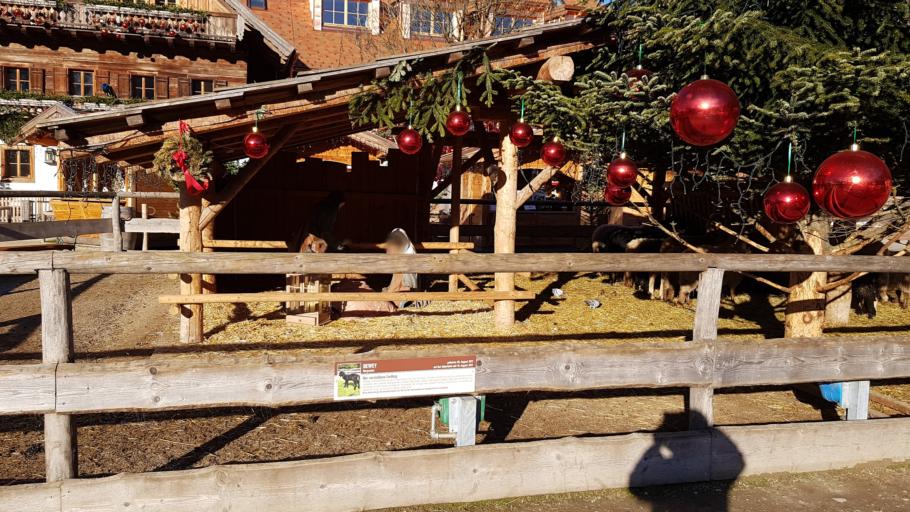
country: AT
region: Salzburg
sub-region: Politischer Bezirk Salzburg-Umgebung
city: Henndorf am Wallersee
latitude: 47.8933
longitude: 13.2206
